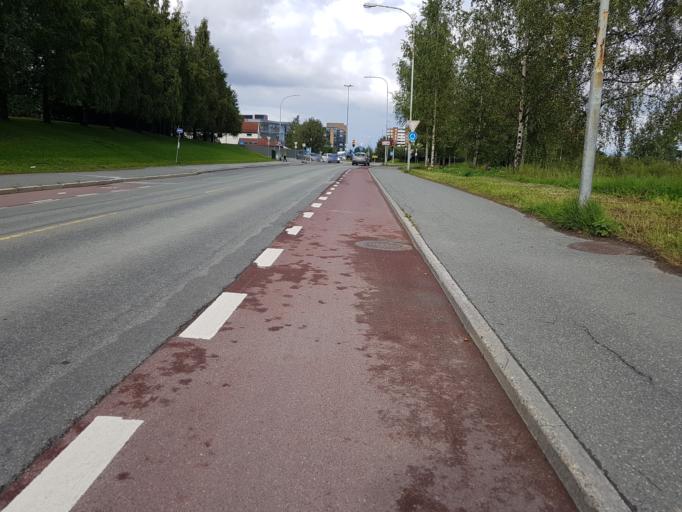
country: NO
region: Sor-Trondelag
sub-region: Trondheim
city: Trondheim
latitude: 63.4189
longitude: 10.4359
